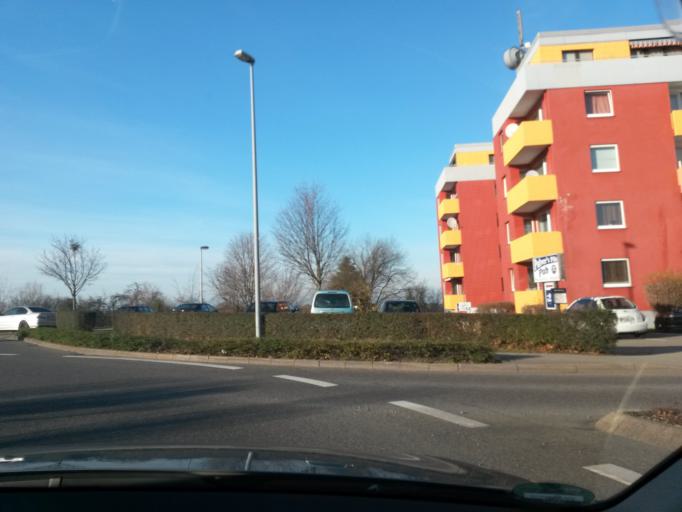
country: DE
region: Baden-Wuerttemberg
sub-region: Karlsruhe Region
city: Birkenfeld
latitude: 48.8704
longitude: 8.6259
